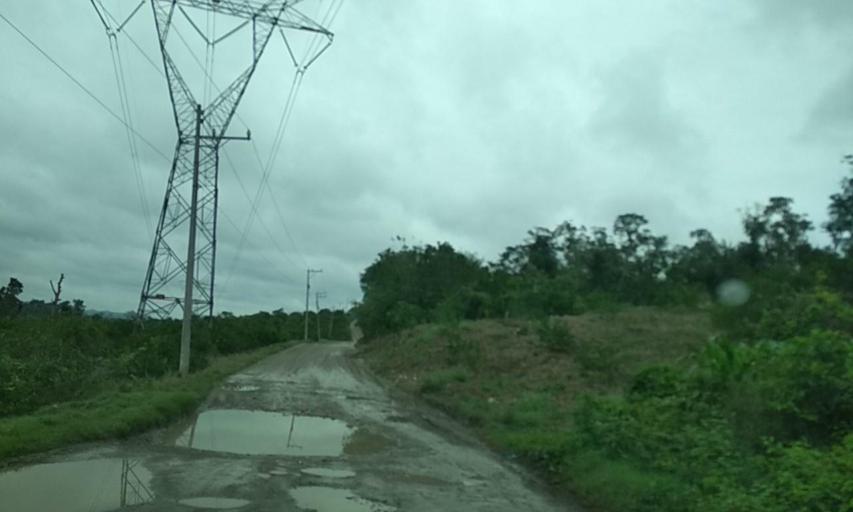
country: MX
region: Puebla
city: Espinal
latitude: 20.3121
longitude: -97.4150
